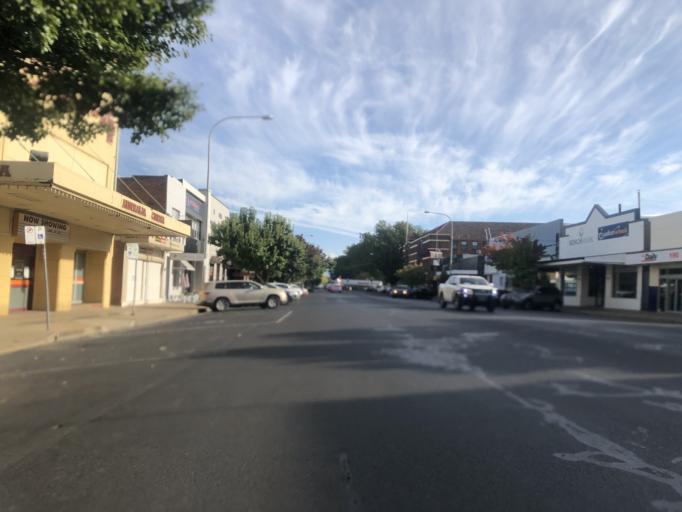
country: AU
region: New South Wales
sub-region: Orange Municipality
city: Orange
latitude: -33.2853
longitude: 149.1008
